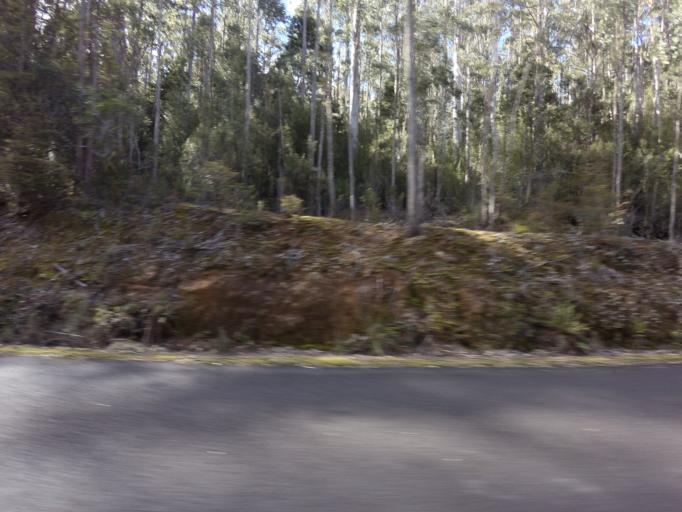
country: AU
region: Tasmania
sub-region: Huon Valley
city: Geeveston
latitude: -42.8254
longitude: 146.3291
